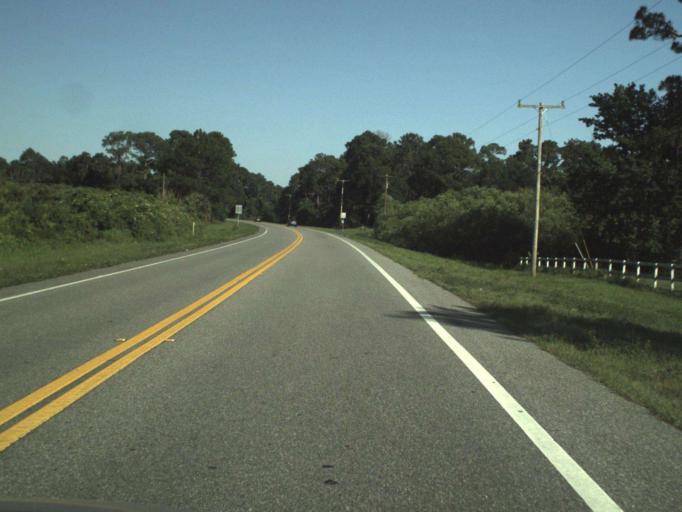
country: US
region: Florida
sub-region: Seminole County
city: Geneva
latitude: 28.7304
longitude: -81.1116
